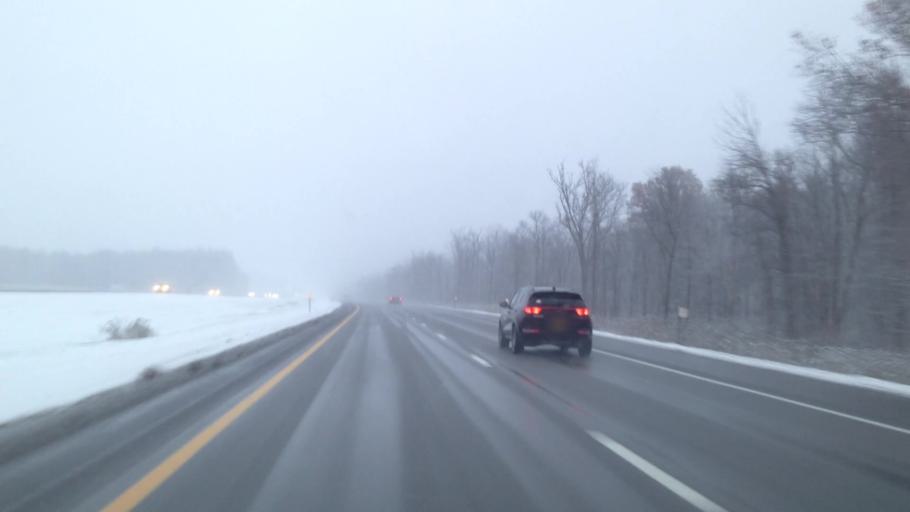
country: US
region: New York
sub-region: Madison County
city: Bolivar
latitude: 43.0912
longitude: -75.9242
